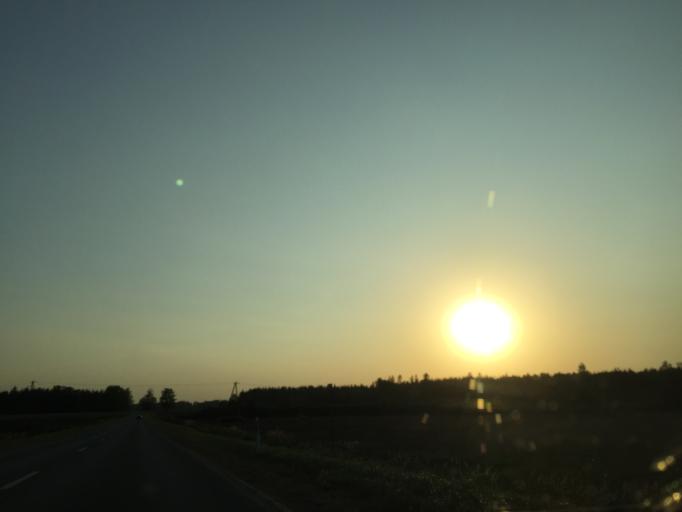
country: LV
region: Lielvarde
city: Lielvarde
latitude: 56.7765
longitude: 24.7815
